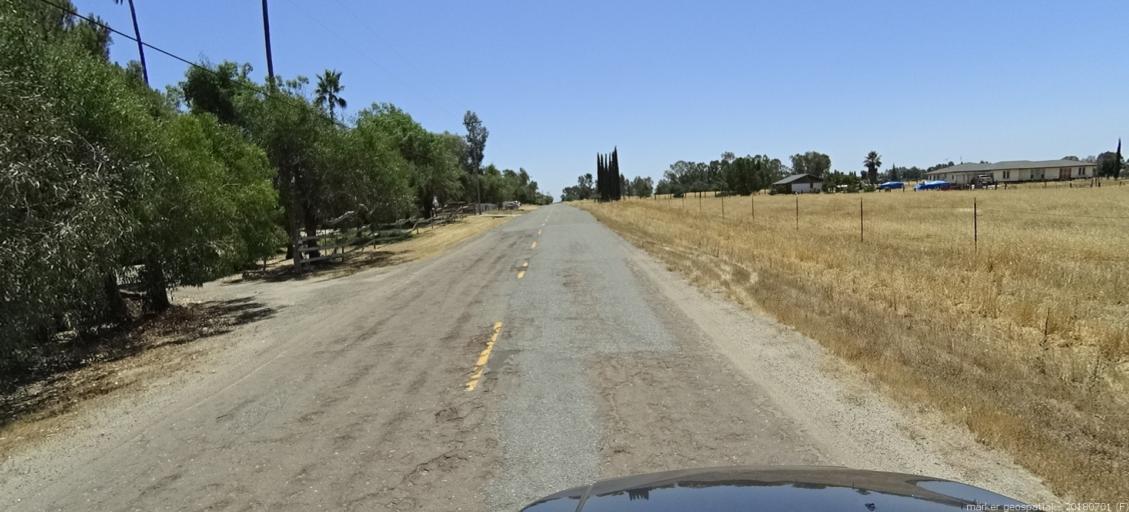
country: US
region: California
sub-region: Madera County
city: Madera Acres
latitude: 37.0450
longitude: -119.9897
